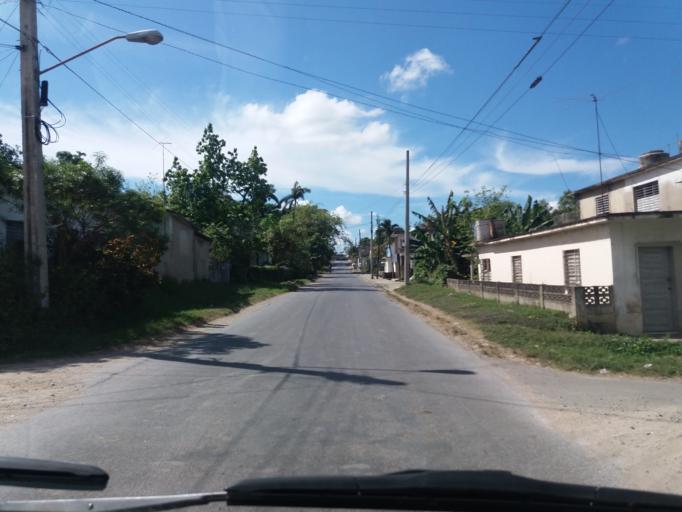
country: CU
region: Cienfuegos
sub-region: Municipio de Cienfuegos
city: Cienfuegos
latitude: 22.1494
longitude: -80.4269
